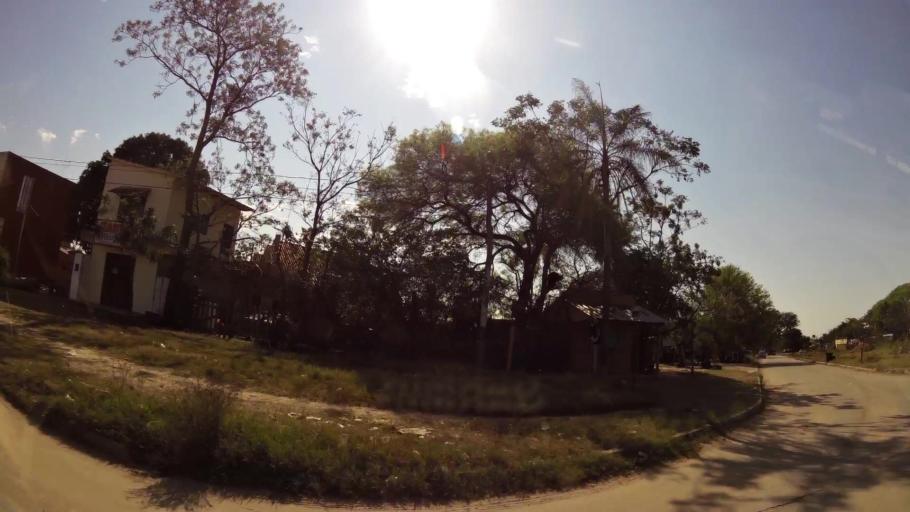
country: BO
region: Santa Cruz
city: Santa Cruz de la Sierra
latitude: -17.7588
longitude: -63.1084
